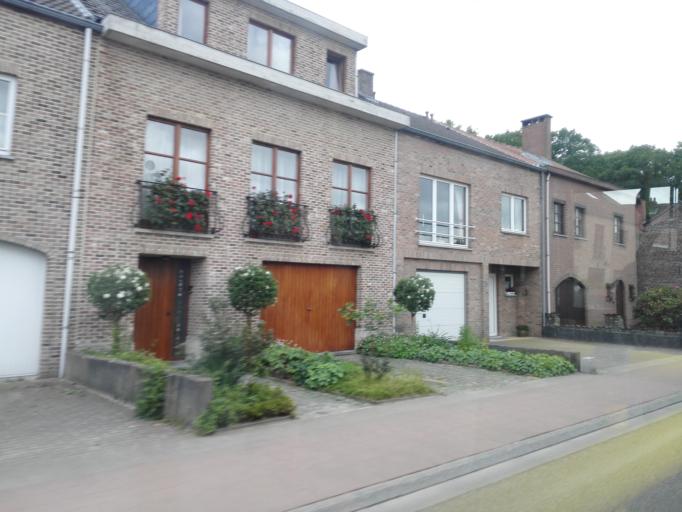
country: BE
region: Flanders
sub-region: Provincie Vlaams-Brabant
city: Tervuren
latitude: 50.8168
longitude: 4.5361
